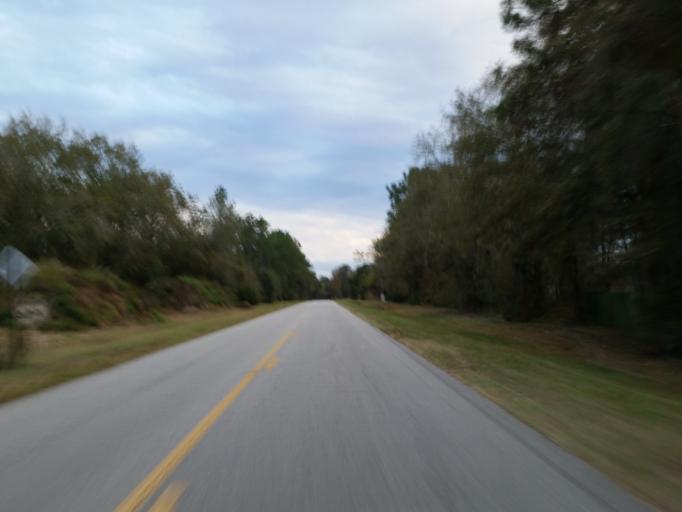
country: US
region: Georgia
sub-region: Echols County
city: Statenville
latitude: 30.5701
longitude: -83.0981
